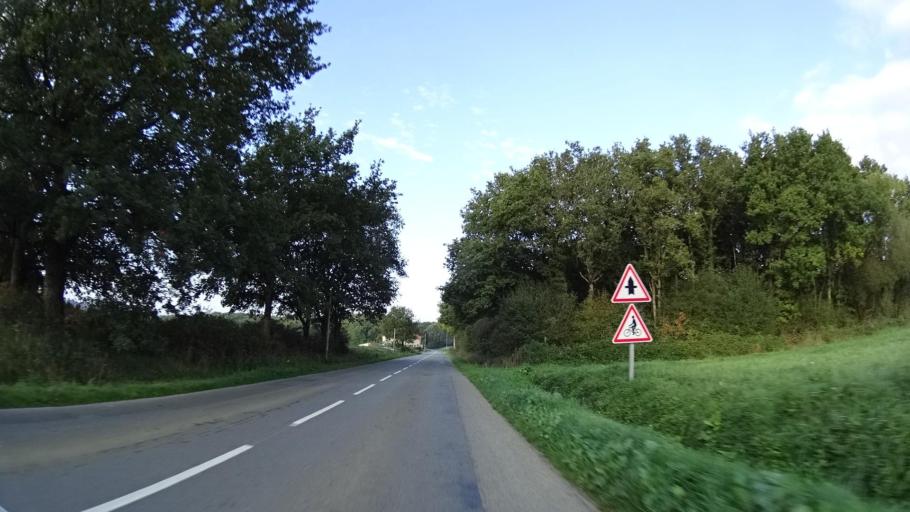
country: FR
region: Brittany
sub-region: Departement des Cotes-d'Armor
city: Plouasne
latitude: 48.2753
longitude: -2.0281
